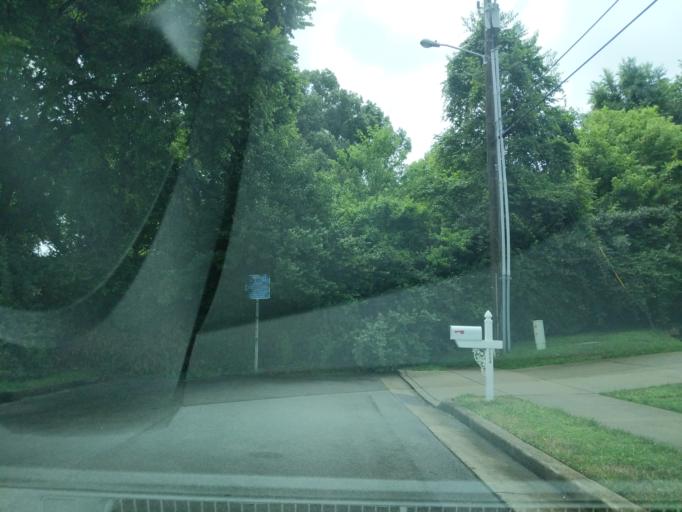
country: US
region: Tennessee
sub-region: Davidson County
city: Lakewood
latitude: 36.2323
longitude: -86.6913
